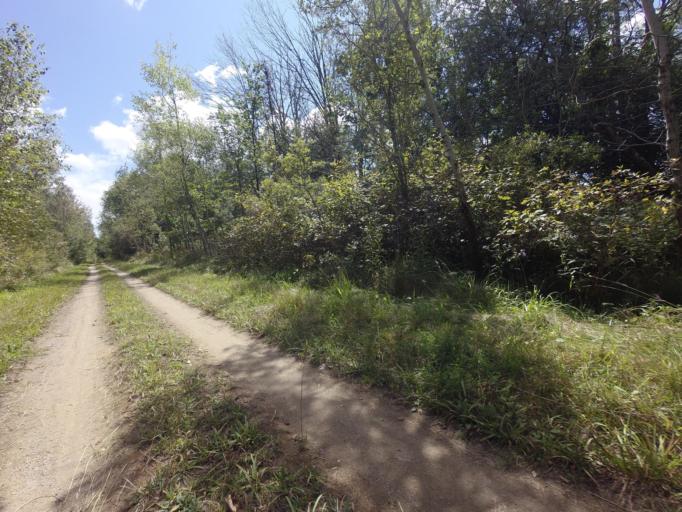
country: CA
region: Ontario
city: Orangeville
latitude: 43.7933
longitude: -80.2708
